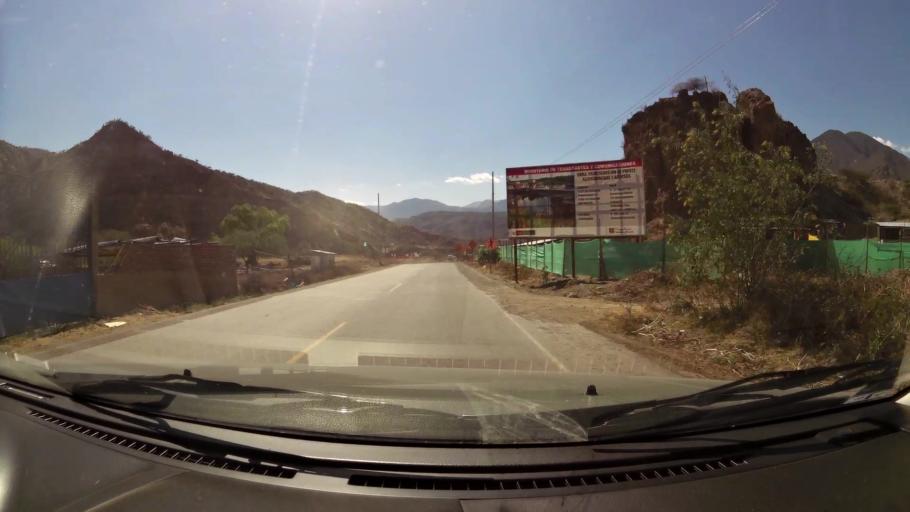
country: PE
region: Huancavelica
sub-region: Provincia de Acobamba
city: Marcas
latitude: -12.8509
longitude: -74.3317
